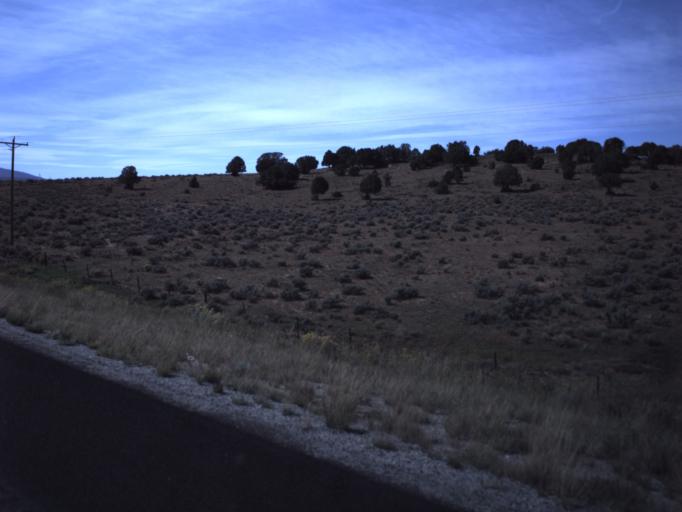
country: US
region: Utah
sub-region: San Juan County
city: Monticello
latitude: 37.8729
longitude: -109.2698
